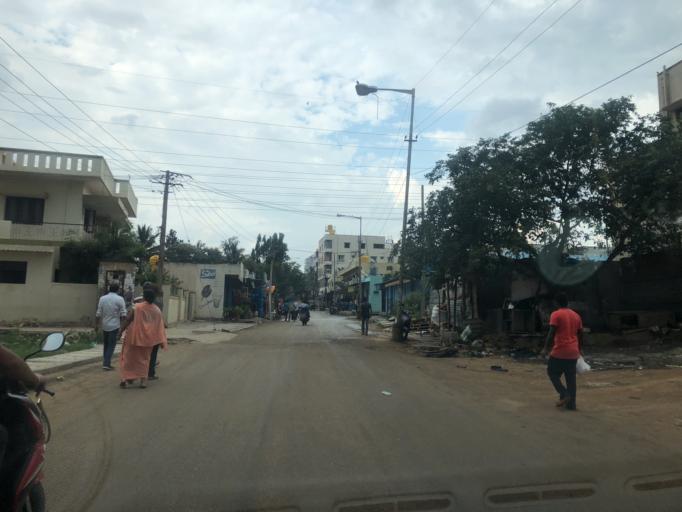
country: IN
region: Karnataka
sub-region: Bangalore Urban
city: Bangalore
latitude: 12.9881
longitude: 77.6972
